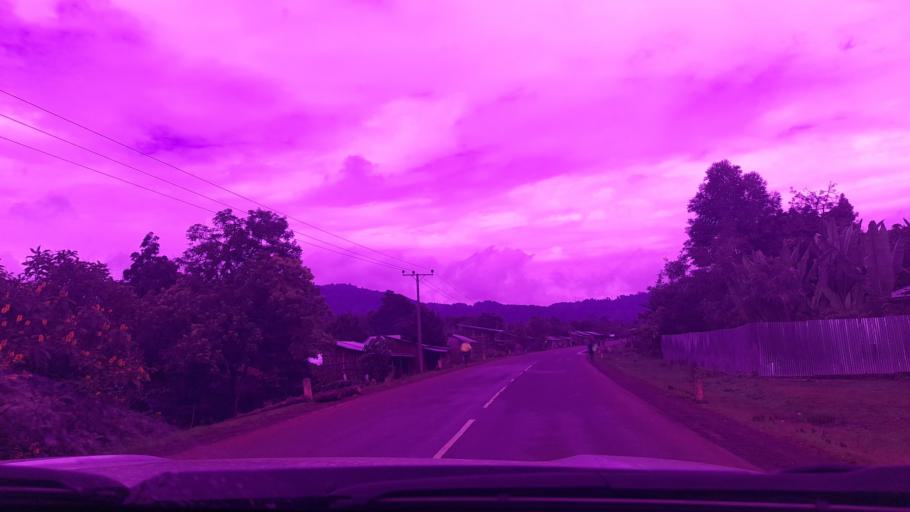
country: ET
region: Oromiya
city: Jima
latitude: 7.5549
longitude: 36.6170
